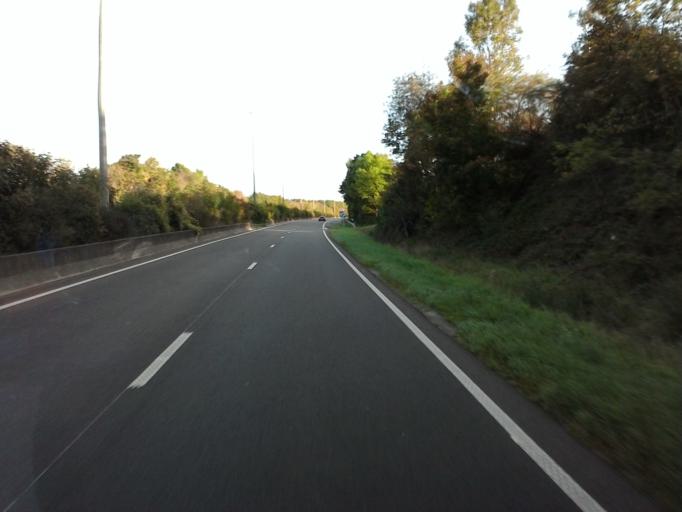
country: BE
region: Wallonia
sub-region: Province de Namur
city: Somme-Leuze
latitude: 50.3063
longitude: 5.3450
